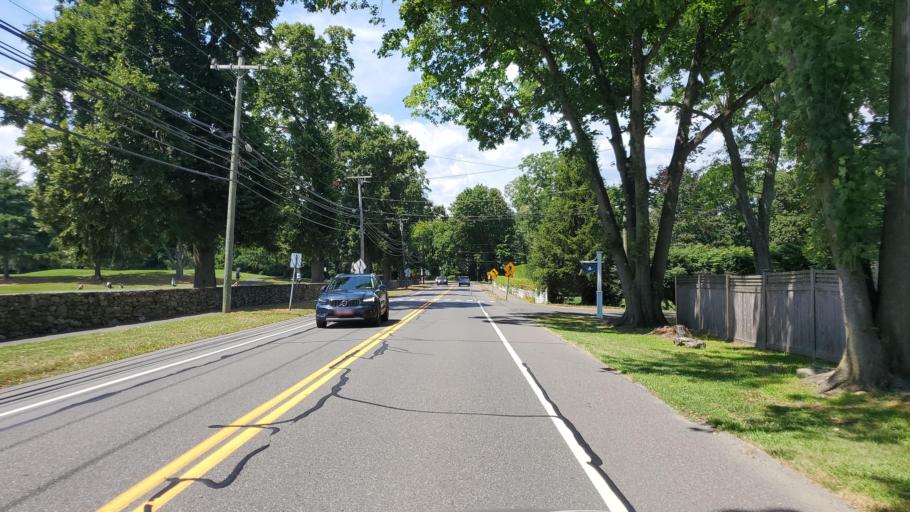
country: US
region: Connecticut
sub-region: Fairfield County
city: Westport
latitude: 41.1143
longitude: -73.3583
